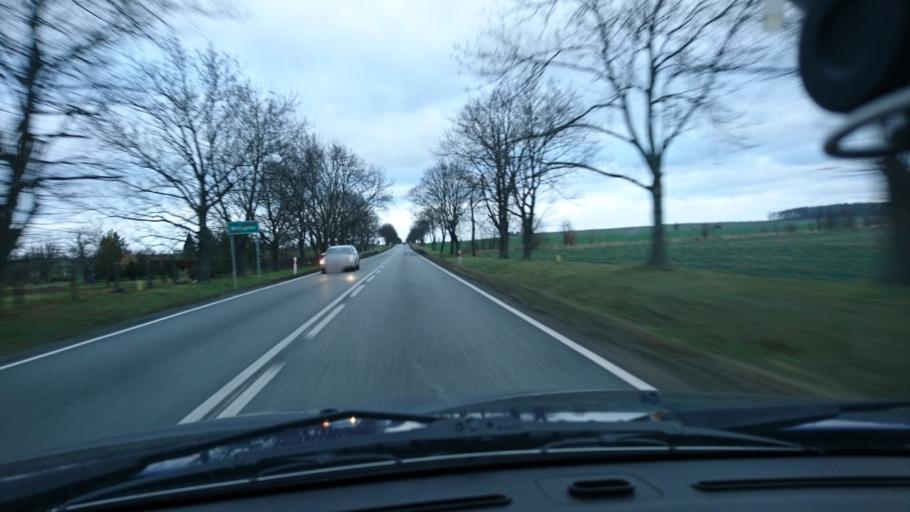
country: PL
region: Opole Voivodeship
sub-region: Powiat kluczborski
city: Byczyna
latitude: 51.0852
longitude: 18.1985
